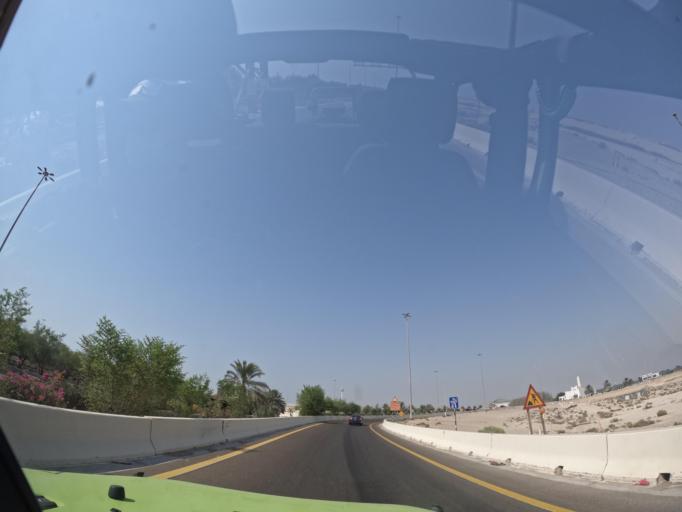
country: AE
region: Abu Dhabi
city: Abu Dhabi
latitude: 24.4629
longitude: 54.6779
